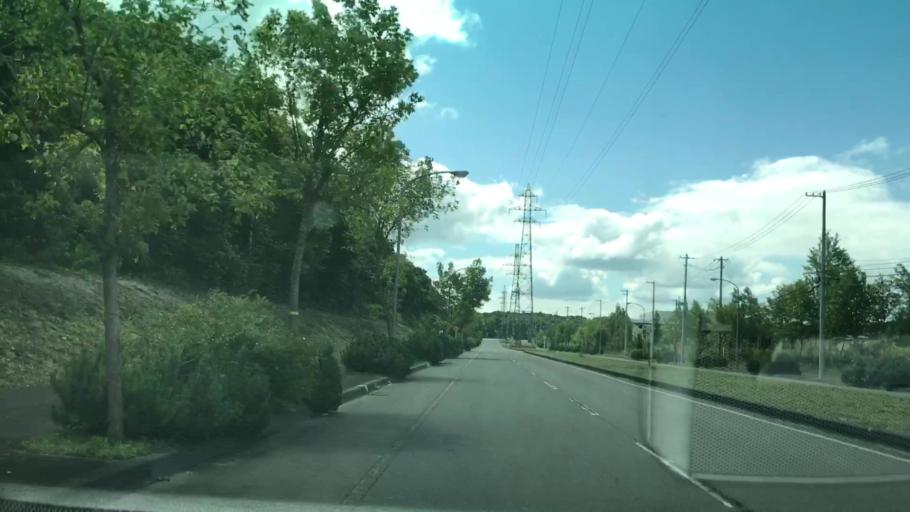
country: JP
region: Hokkaido
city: Chitose
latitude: 42.7770
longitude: 141.6166
